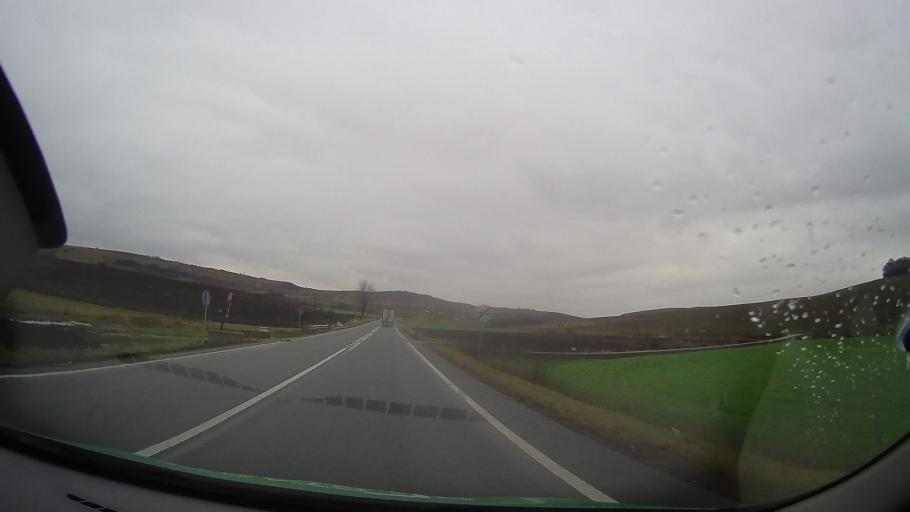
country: RO
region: Mures
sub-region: Comuna Lunca
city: Lunca
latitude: 46.8749
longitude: 24.5447
